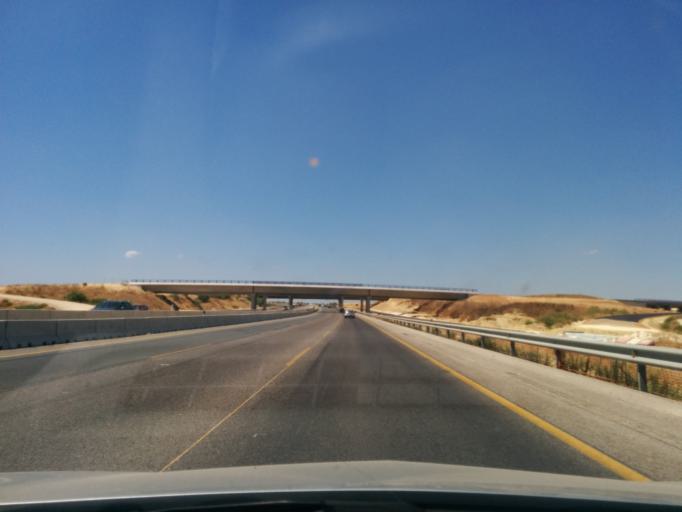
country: ES
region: Andalusia
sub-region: Provincia de Sevilla
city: Gines
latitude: 37.3708
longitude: -6.0993
